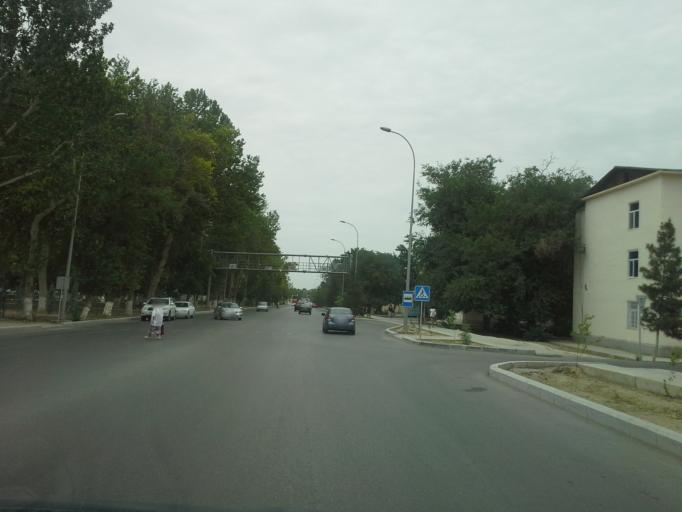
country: TM
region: Ahal
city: Ashgabat
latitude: 37.9138
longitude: 58.4060
